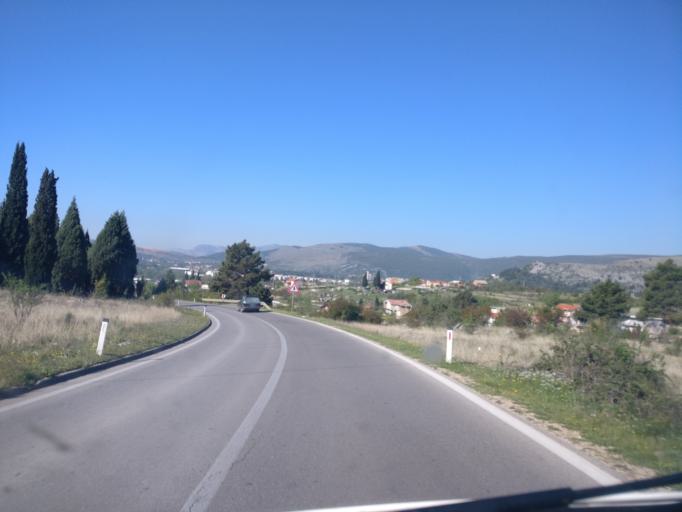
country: BA
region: Federation of Bosnia and Herzegovina
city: Tasovcici
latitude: 43.1186
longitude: 17.7237
